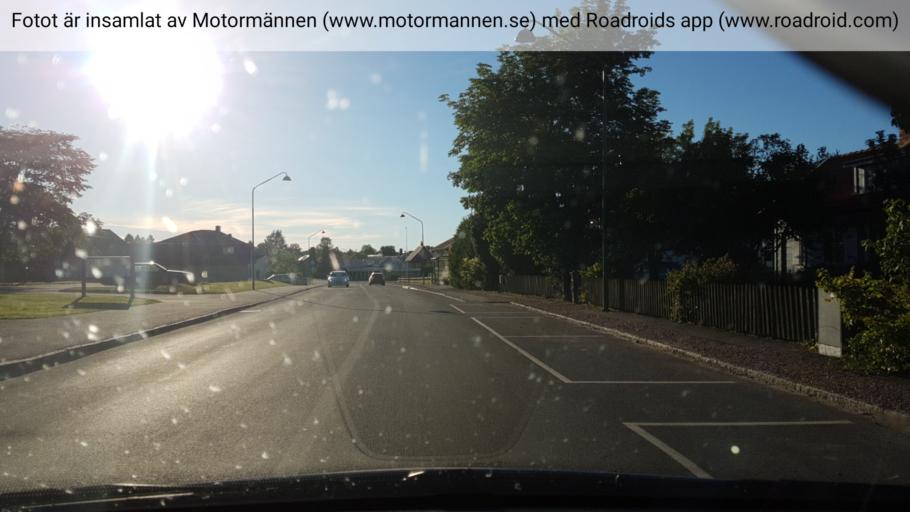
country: SE
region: Vaestra Goetaland
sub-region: Tidaholms Kommun
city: Tidaholm
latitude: 58.1860
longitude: 13.9585
